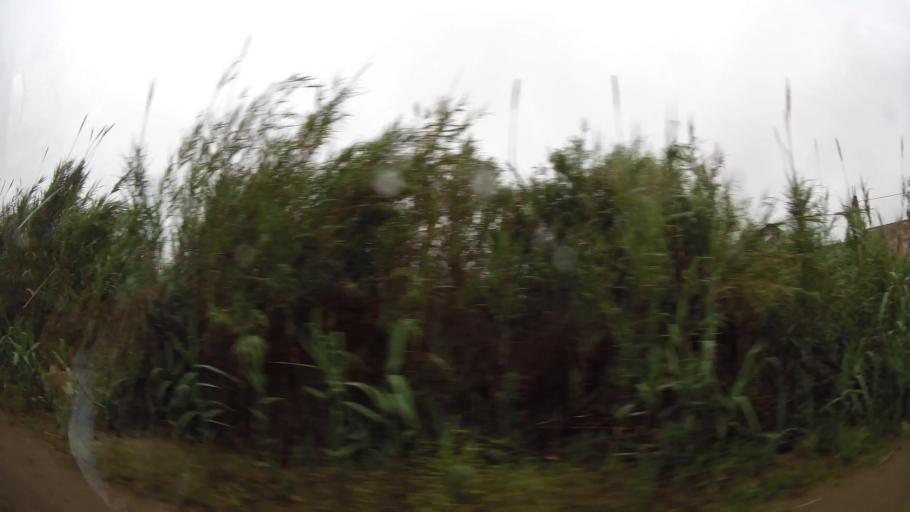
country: MA
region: Oriental
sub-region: Nador
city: Boudinar
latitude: 35.1158
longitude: -3.5766
